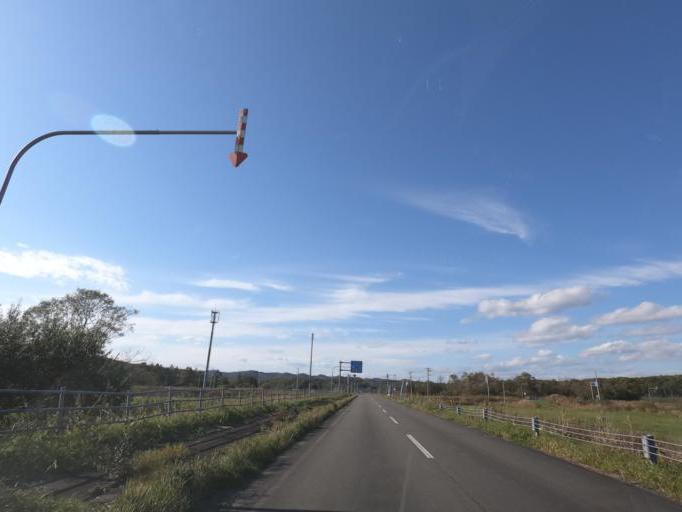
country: JP
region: Hokkaido
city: Obihiro
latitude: 42.6407
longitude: 143.5078
